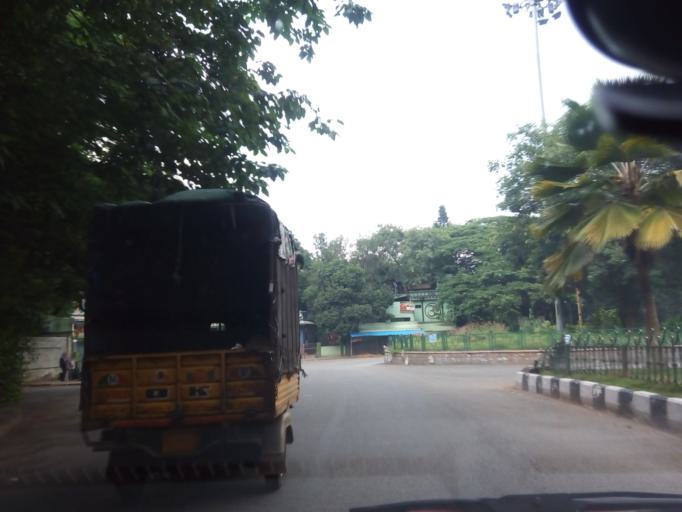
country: IN
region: Karnataka
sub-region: Bangalore Urban
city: Bangalore
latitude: 13.0123
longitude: 77.5688
